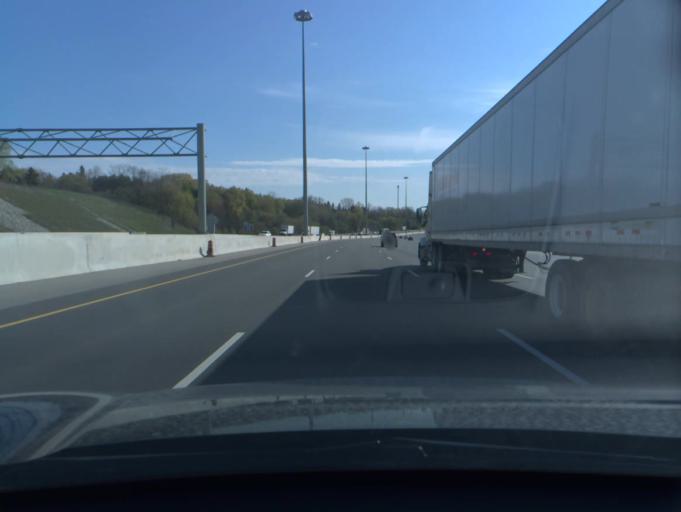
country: CA
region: Ontario
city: North Perth
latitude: 43.8211
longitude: -81.0000
